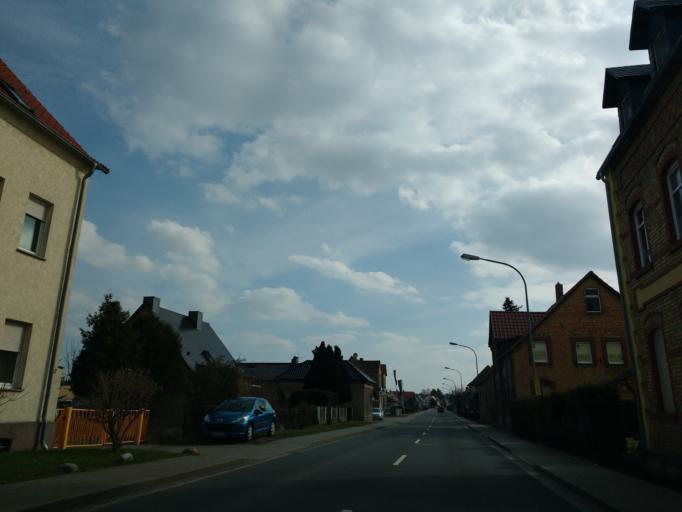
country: DE
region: Saxony-Anhalt
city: Roblingen am See
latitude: 51.4599
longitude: 11.6713
